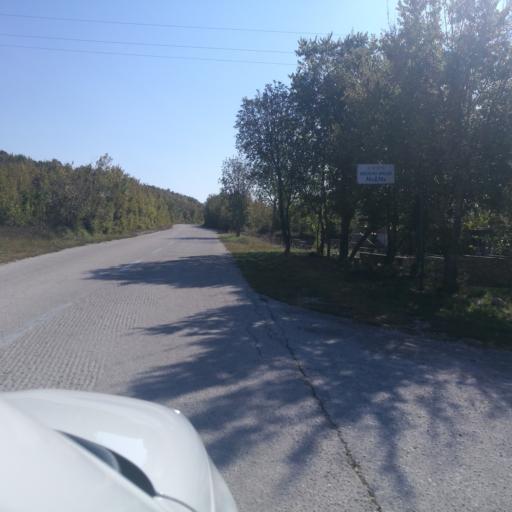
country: HR
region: Splitsko-Dalmatinska
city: Trilj
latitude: 43.5231
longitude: 16.7495
